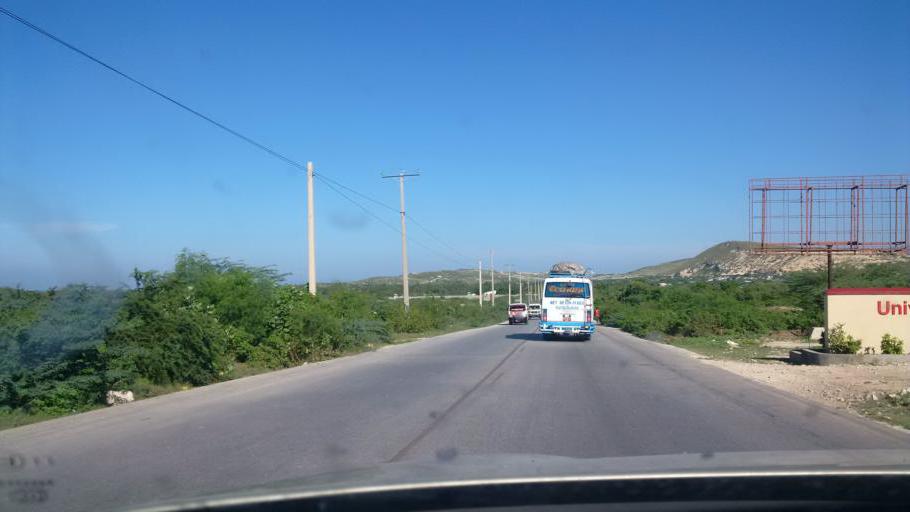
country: HT
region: Ouest
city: Cabaret
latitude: 18.7142
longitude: -72.3589
